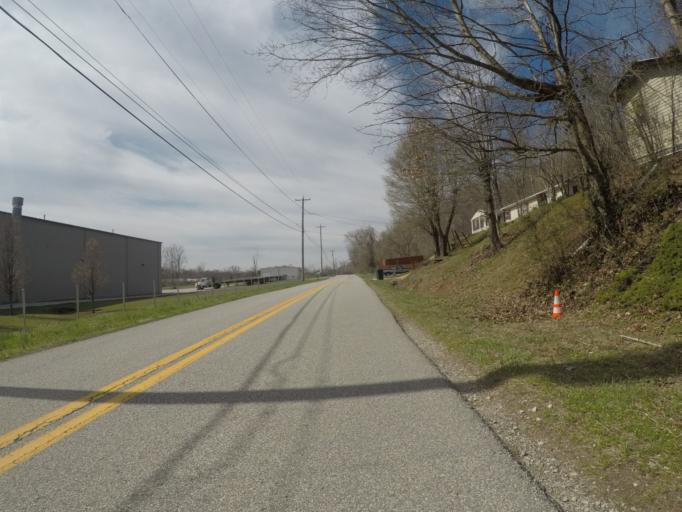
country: US
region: West Virginia
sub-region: Cabell County
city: Pea Ridge
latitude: 38.4211
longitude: -82.3474
